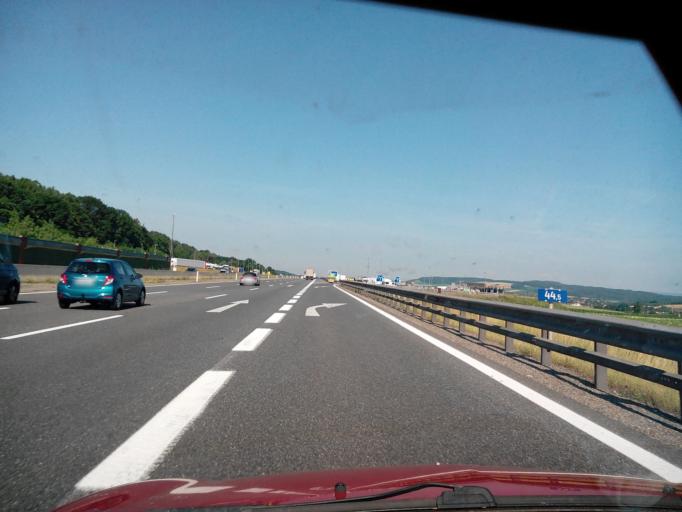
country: AT
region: Lower Austria
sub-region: Politischer Bezirk Sankt Polten
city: Kirchstetten
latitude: 48.1852
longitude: 15.8021
